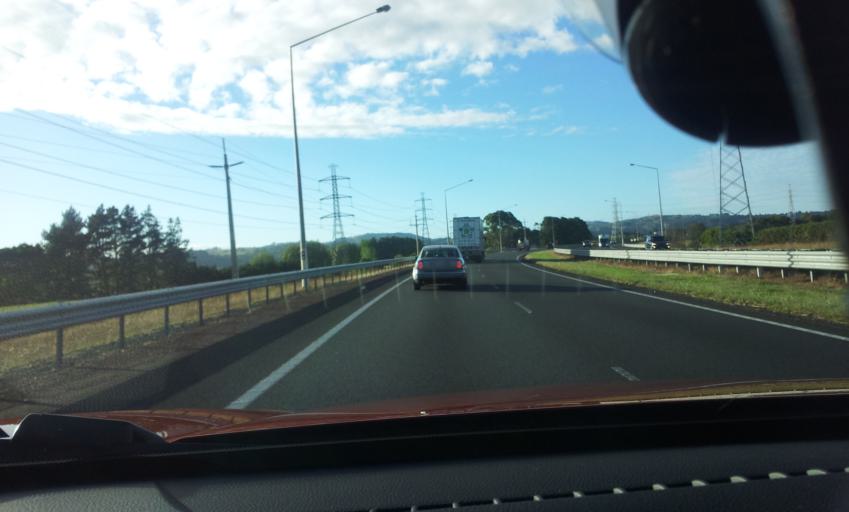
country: NZ
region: Auckland
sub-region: Auckland
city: Papakura
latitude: -37.1190
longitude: 174.9549
